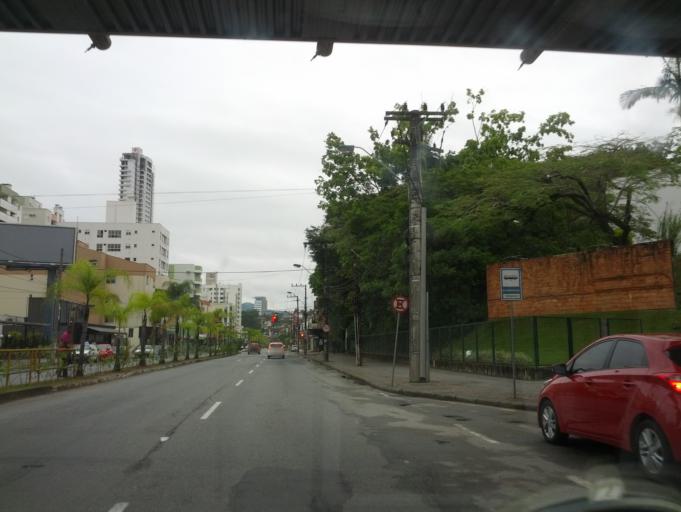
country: BR
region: Santa Catarina
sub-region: Blumenau
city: Blumenau
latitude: -26.9063
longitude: -49.0779
